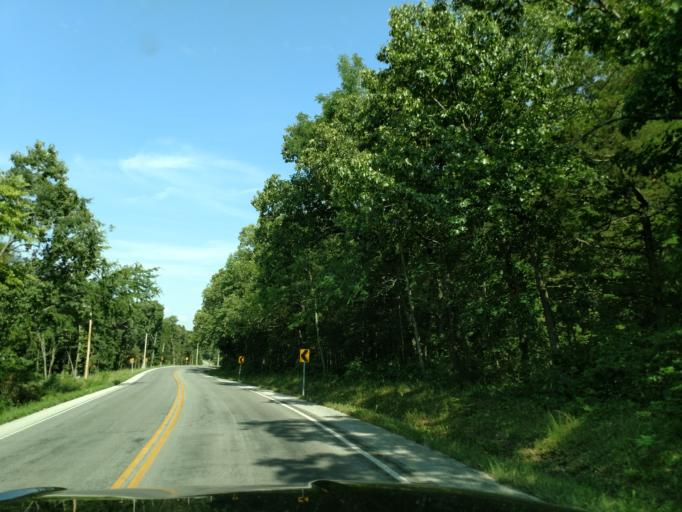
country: US
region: Missouri
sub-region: Barry County
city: Shell Knob
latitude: 36.6100
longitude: -93.5905
